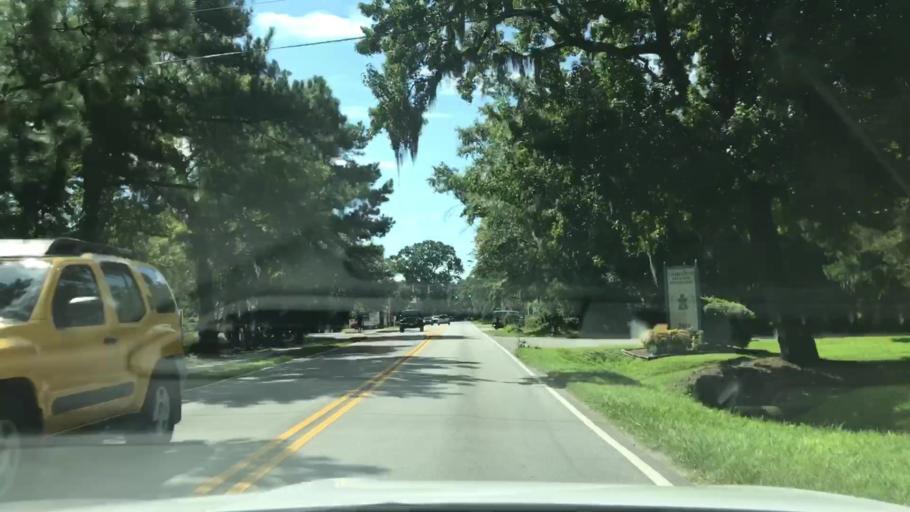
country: US
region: South Carolina
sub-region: Charleston County
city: North Charleston
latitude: 32.8266
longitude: -80.0401
